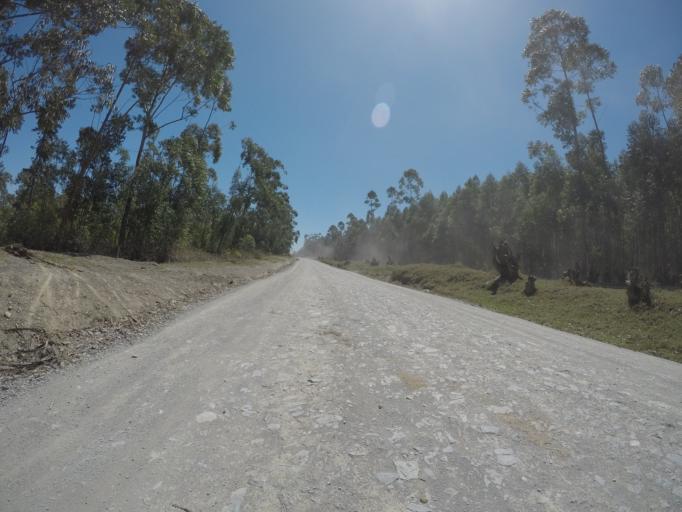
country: ZA
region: Eastern Cape
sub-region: OR Tambo District Municipality
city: Libode
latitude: -31.9603
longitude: 29.0248
